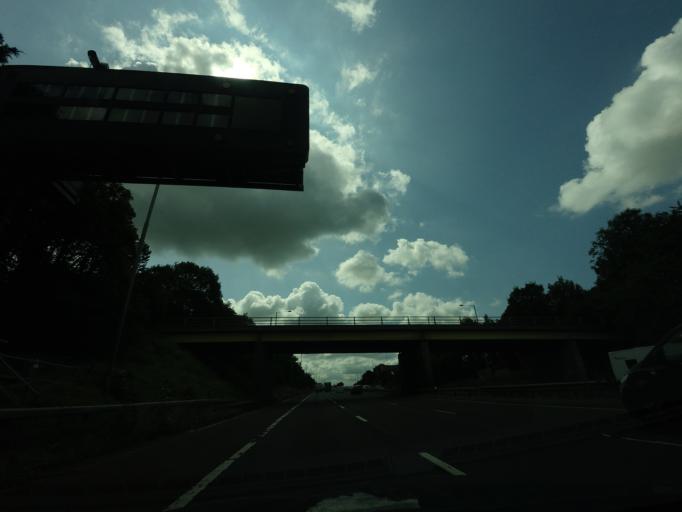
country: GB
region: England
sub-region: Lancashire
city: Euxton
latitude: 53.6513
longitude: -2.6910
